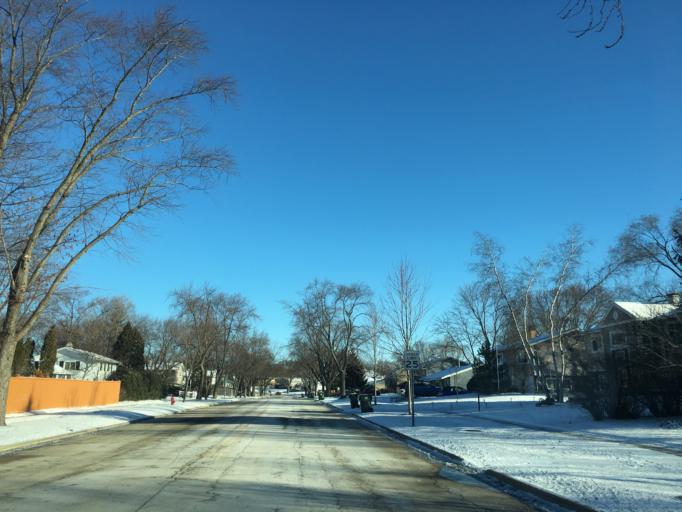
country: US
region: Illinois
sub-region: Cook County
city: Hoffman Estates
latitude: 42.0546
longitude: -88.0914
